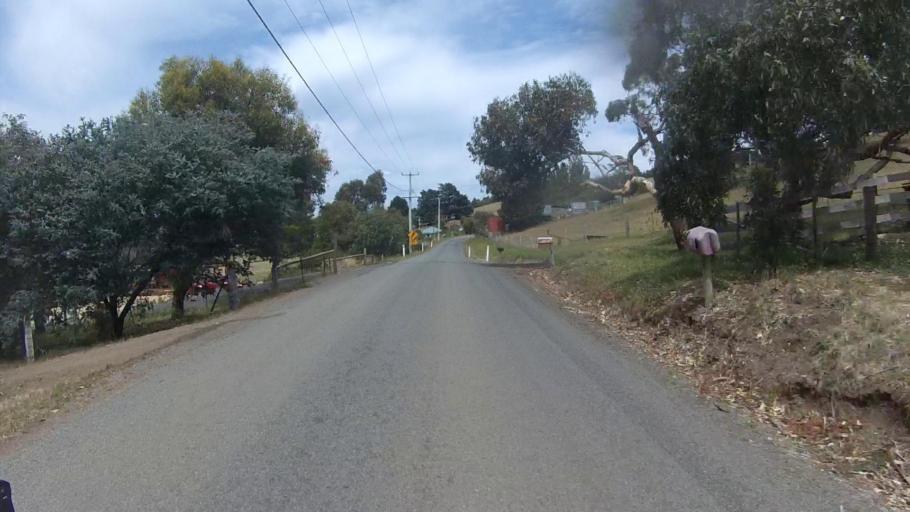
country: AU
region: Tasmania
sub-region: Sorell
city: Sorell
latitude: -42.8066
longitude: 147.8340
